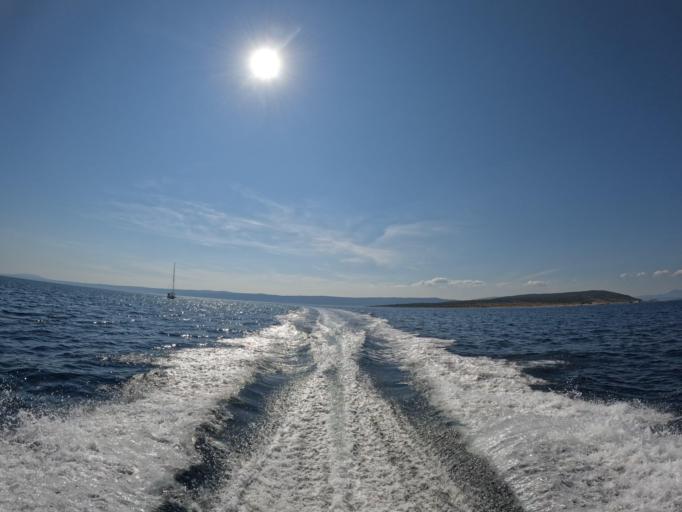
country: HR
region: Primorsko-Goranska
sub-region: Grad Krk
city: Krk
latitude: 44.9541
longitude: 14.5664
